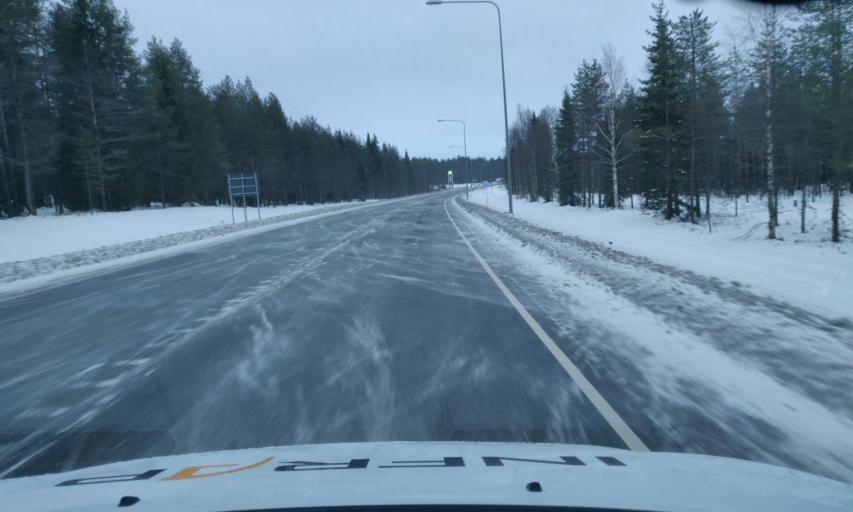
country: FI
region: Northern Ostrobothnia
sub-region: Koillismaa
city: Kuusamo
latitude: 65.9867
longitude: 29.1629
